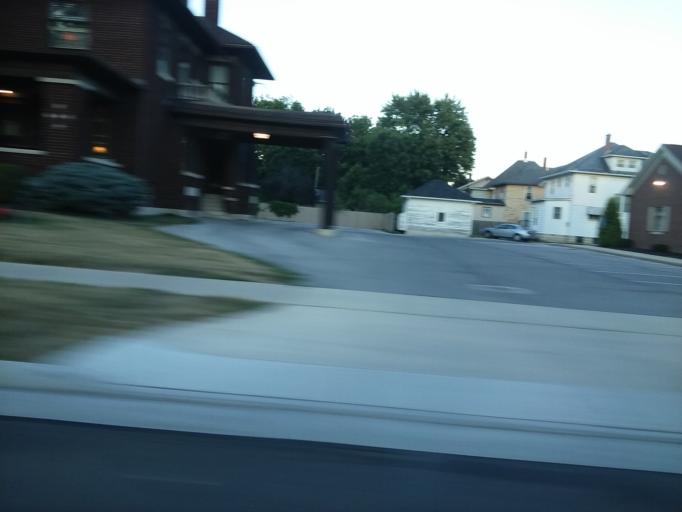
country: US
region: Ohio
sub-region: Hancock County
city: Findlay
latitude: 41.0530
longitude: -83.6500
